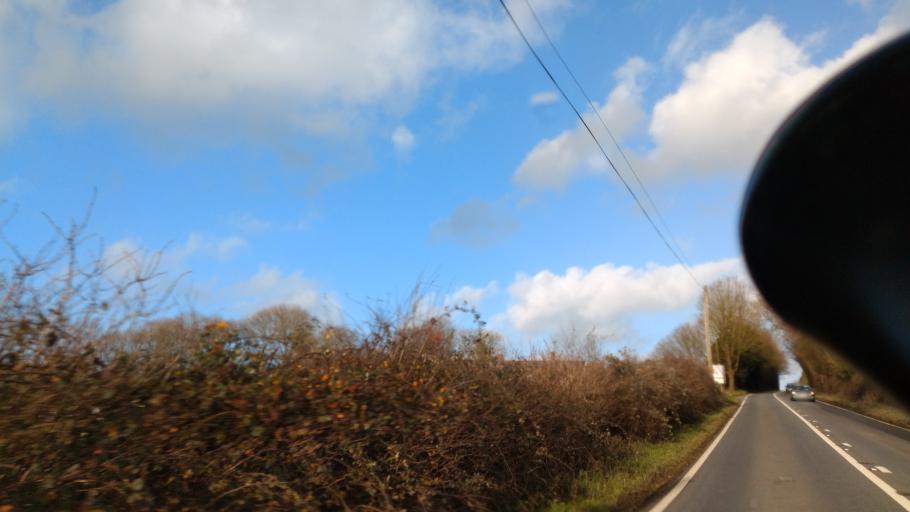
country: GB
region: England
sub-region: Somerset
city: Shepton Mallet
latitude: 51.1630
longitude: -2.5401
